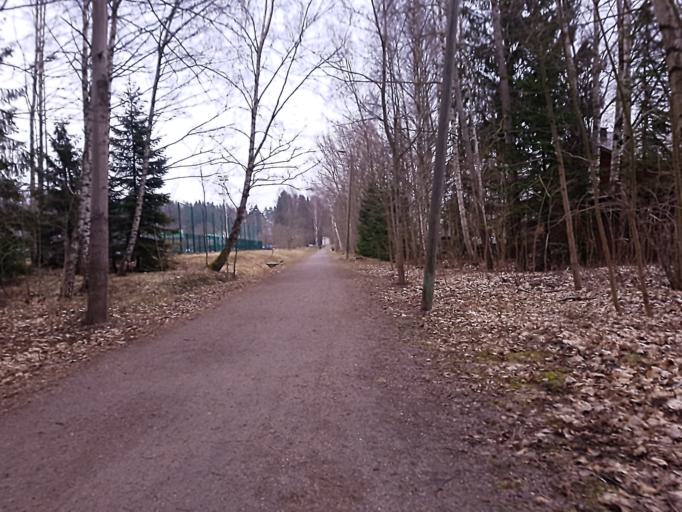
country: FI
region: Uusimaa
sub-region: Helsinki
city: Helsinki
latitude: 60.2460
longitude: 24.9208
